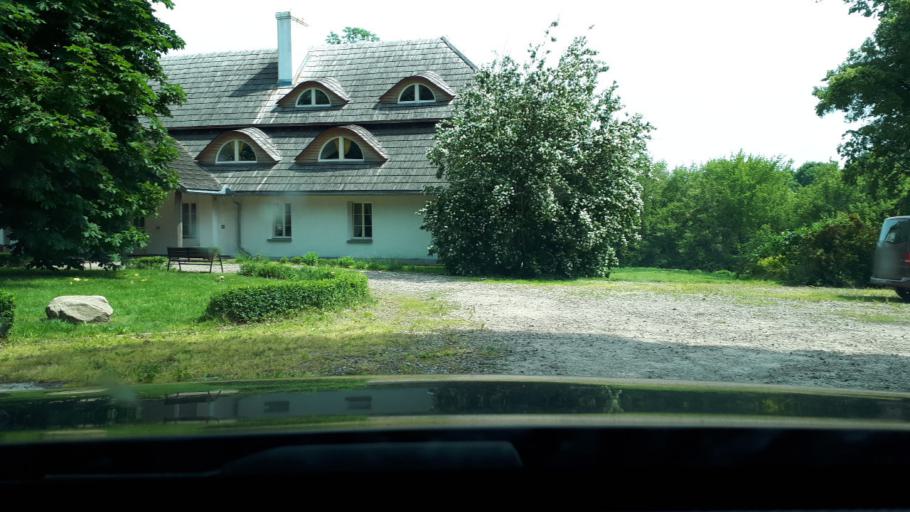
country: PL
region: Masovian Voivodeship
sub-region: Powiat sochaczewski
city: Teresin
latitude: 52.2585
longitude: 20.3580
